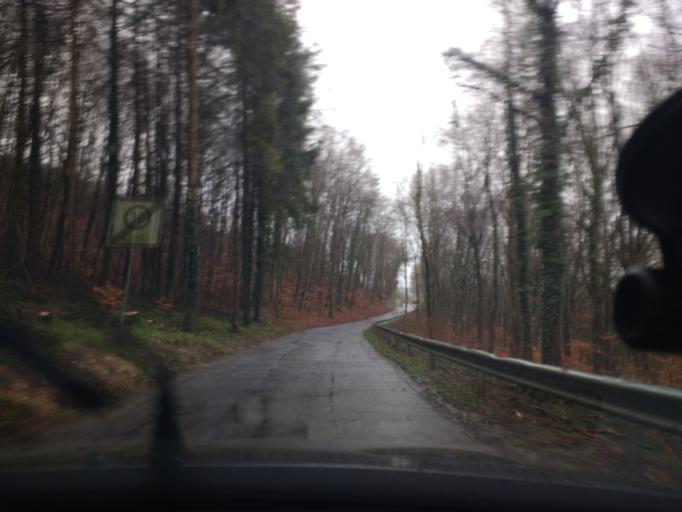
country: LU
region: Grevenmacher
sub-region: Canton de Grevenmacher
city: Grevenmacher
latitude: 49.6720
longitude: 6.4486
